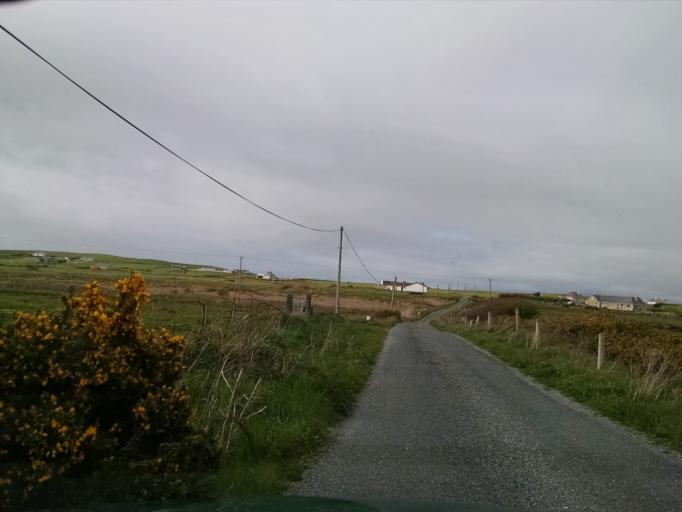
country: IE
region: Connaught
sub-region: County Galway
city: Clifden
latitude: 53.7538
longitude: -9.8854
